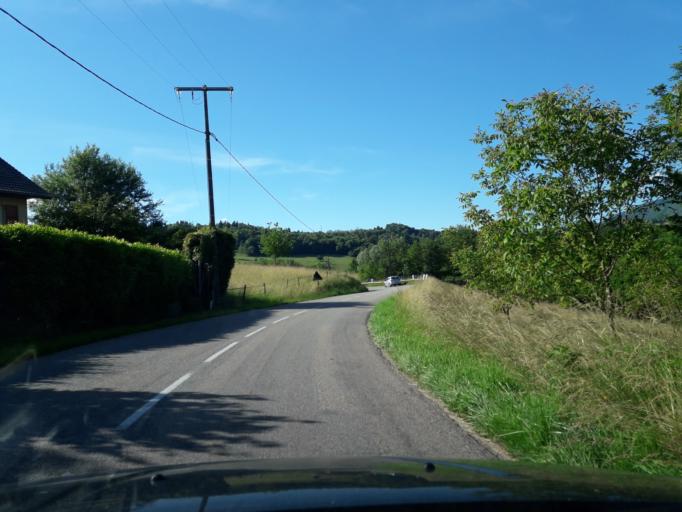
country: FR
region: Rhone-Alpes
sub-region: Departement de la Savoie
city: La Bridoire
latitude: 45.5410
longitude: 5.7723
